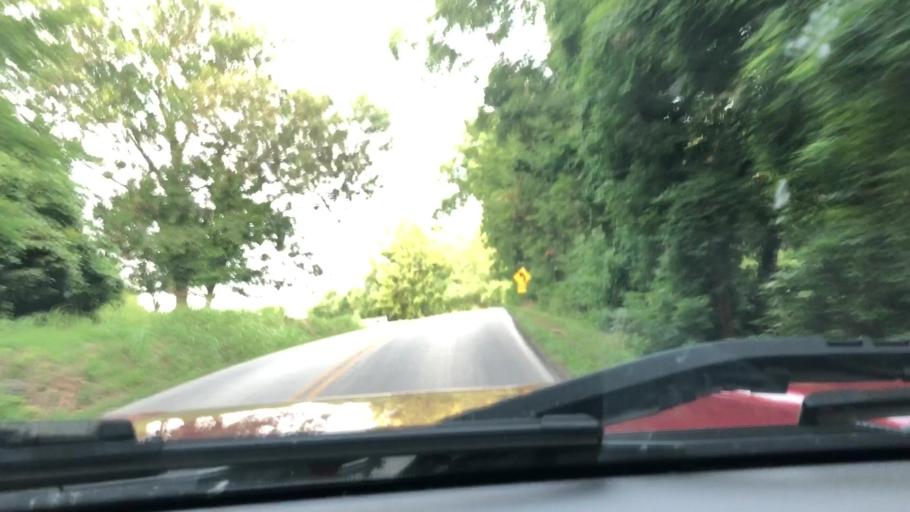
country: US
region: Missouri
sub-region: Jasper County
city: Duquesne
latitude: 37.0152
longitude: -94.4946
